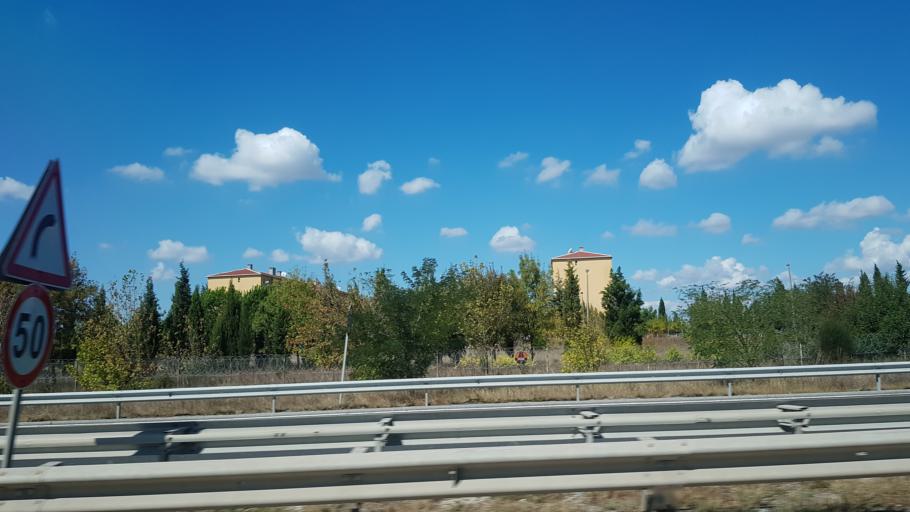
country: TR
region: Tekirdag
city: Velimese
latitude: 41.2219
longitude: 27.8684
